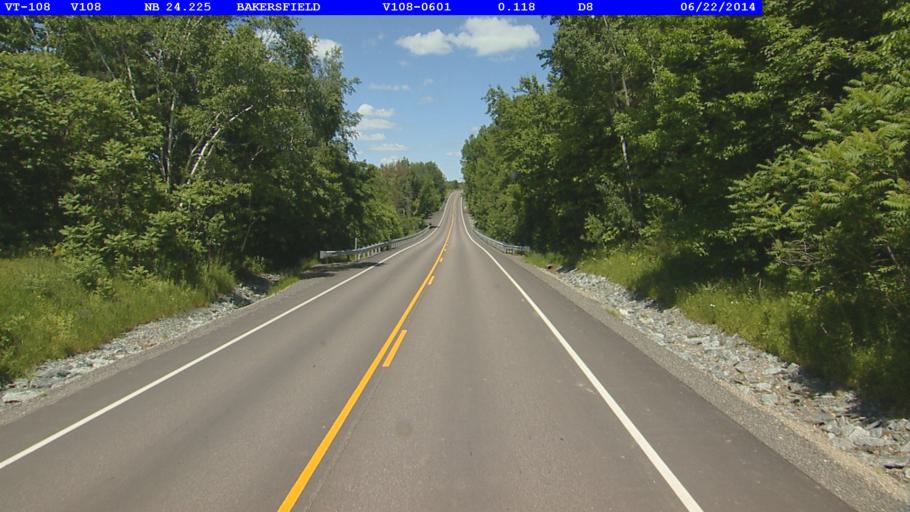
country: US
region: Vermont
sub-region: Franklin County
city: Enosburg Falls
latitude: 44.7353
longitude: -72.8266
